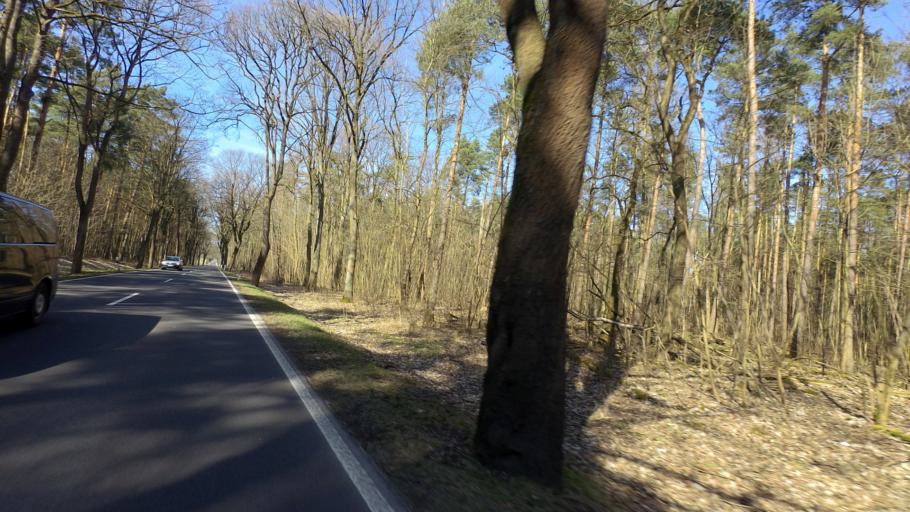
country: DE
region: Brandenburg
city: Waldsieversdorf
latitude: 52.5517
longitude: 14.0426
